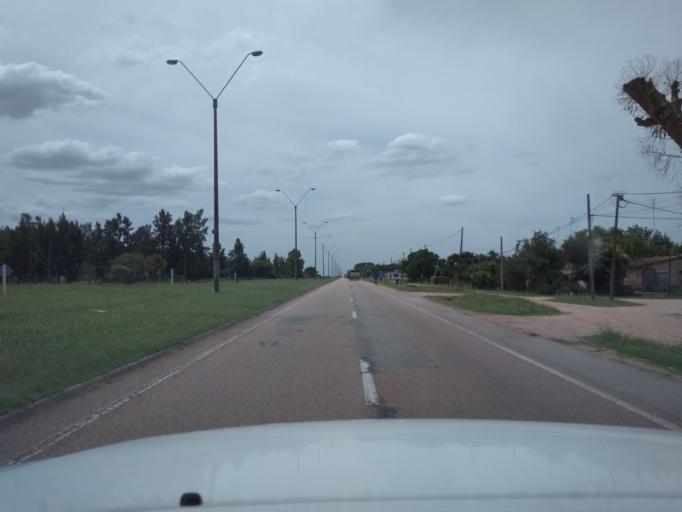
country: UY
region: Canelones
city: Joanico
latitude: -34.5924
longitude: -56.2624
